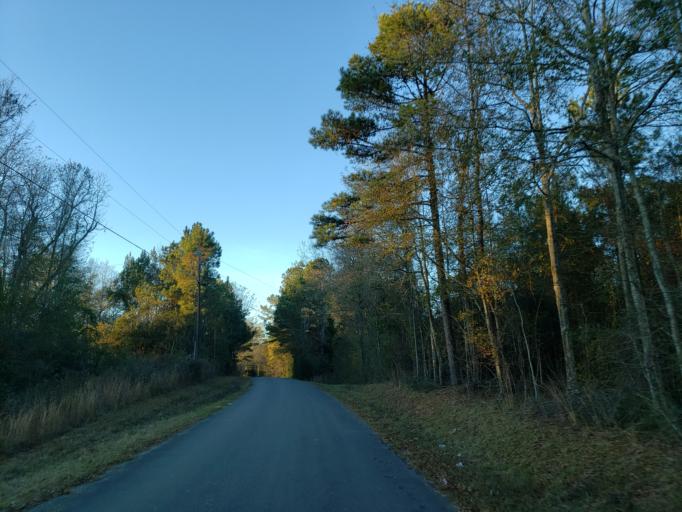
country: US
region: Mississippi
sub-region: Covington County
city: Collins
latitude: 31.5667
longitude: -89.4376
